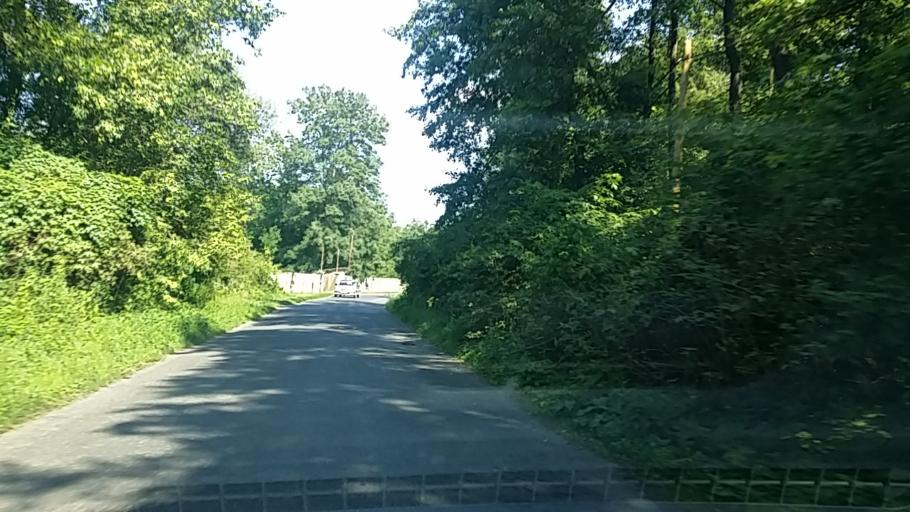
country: HU
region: Zala
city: Lenti
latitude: 46.5556
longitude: 16.5765
